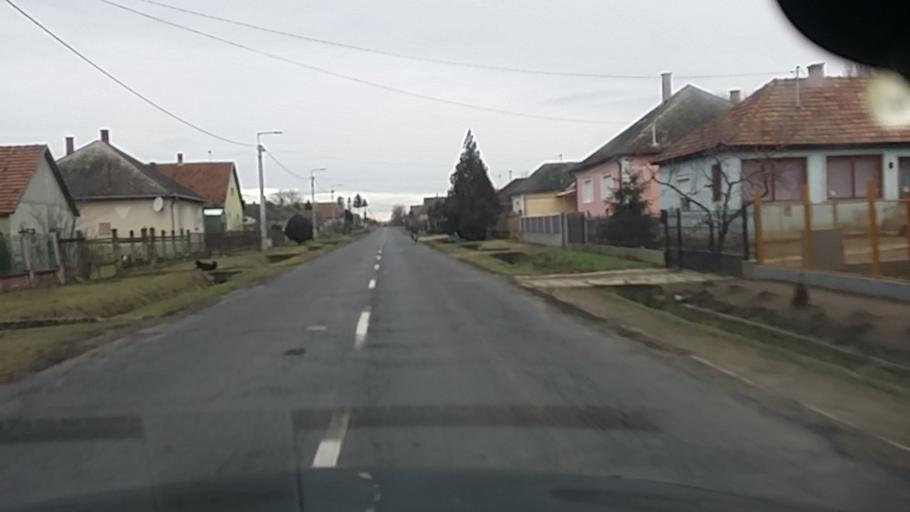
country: HU
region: Szabolcs-Szatmar-Bereg
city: Kek
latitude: 48.1001
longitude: 21.8827
